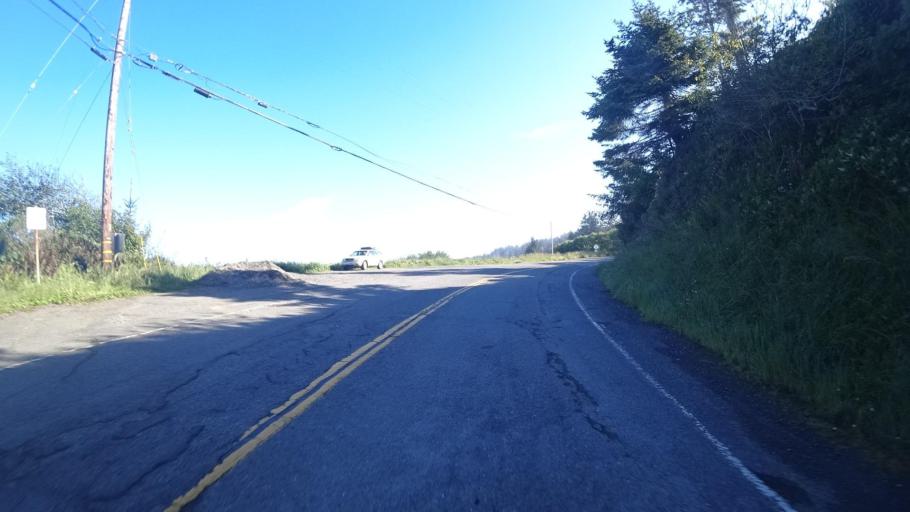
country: US
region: California
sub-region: Humboldt County
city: Westhaven-Moonstone
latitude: 41.1084
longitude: -124.1599
